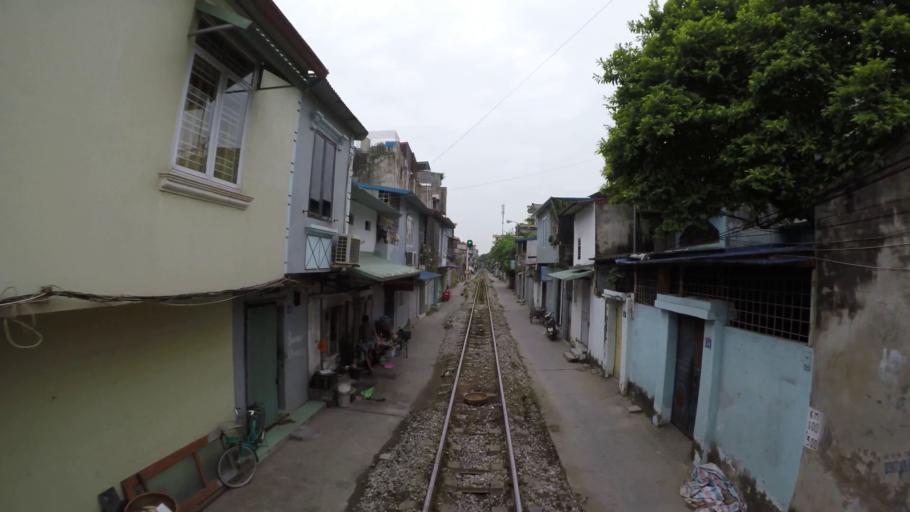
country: VN
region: Hai Phong
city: Haiphong
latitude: 20.8625
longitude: 106.6612
